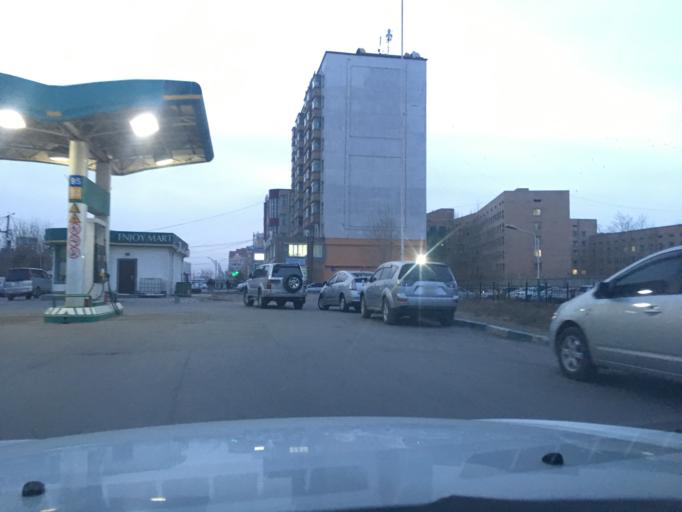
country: MN
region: Ulaanbaatar
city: Ulaanbaatar
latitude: 47.9137
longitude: 106.8598
